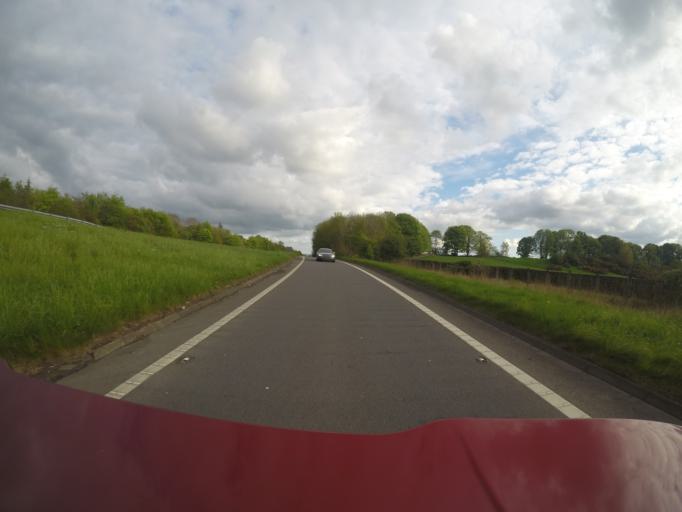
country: GB
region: Scotland
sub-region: Renfrewshire
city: Bishopton
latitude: 55.8997
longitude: -4.4847
